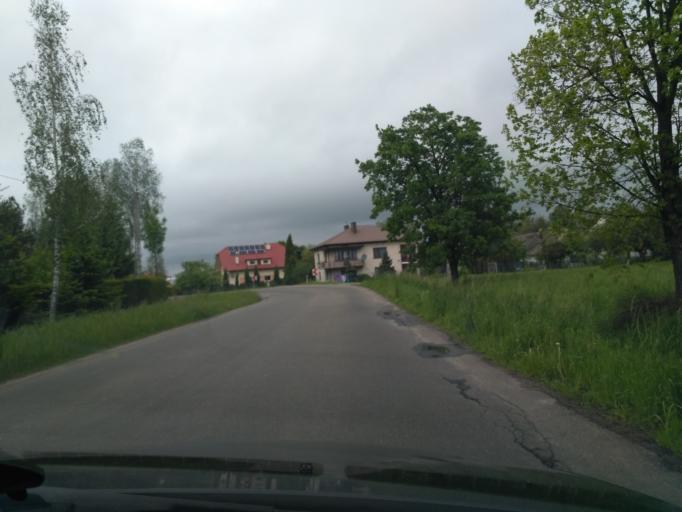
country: PL
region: Subcarpathian Voivodeship
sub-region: Powiat jasielski
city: Brzyska
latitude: 49.8208
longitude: 21.3960
